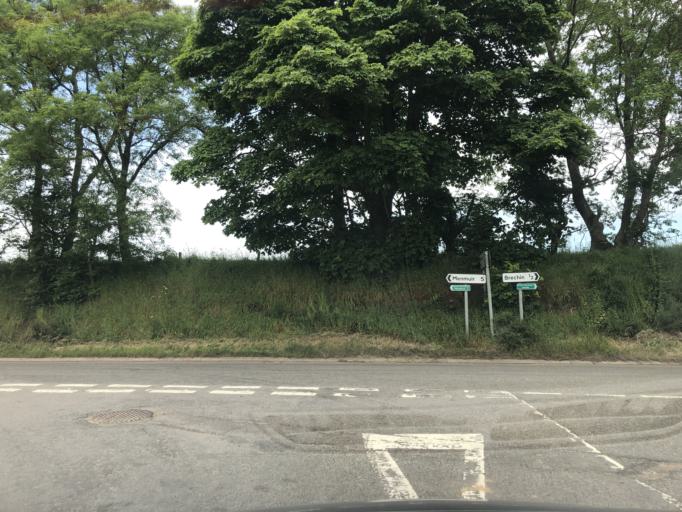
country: GB
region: Scotland
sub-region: Angus
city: Brechin
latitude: 56.7375
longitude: -2.6799
